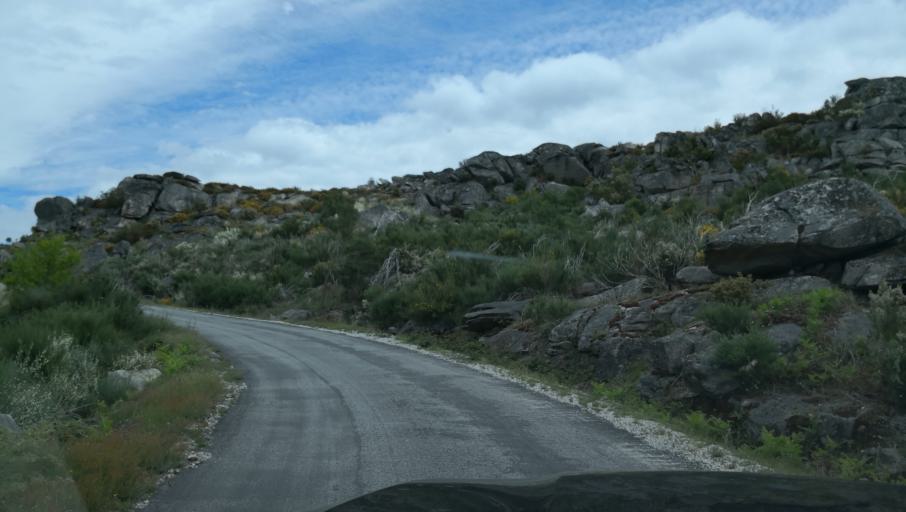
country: PT
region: Vila Real
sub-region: Vila Real
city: Vila Real
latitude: 41.3717
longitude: -7.6975
